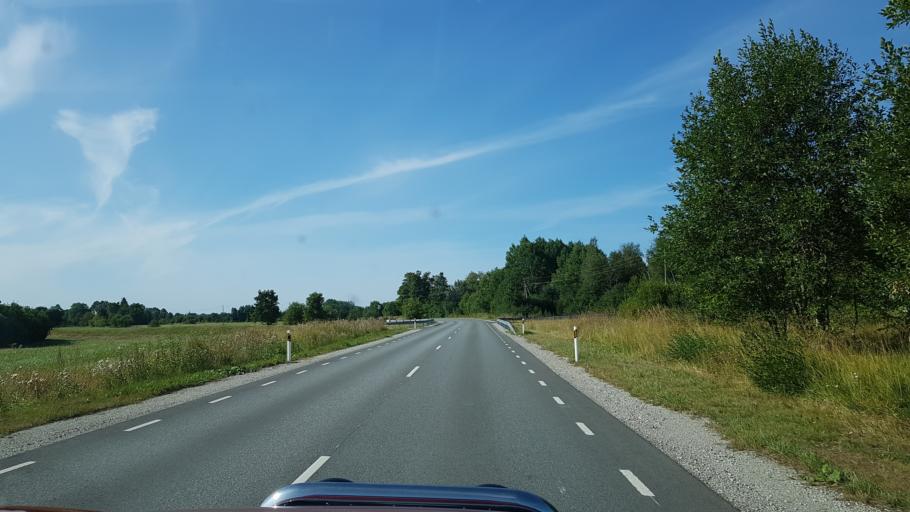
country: EE
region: Harju
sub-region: Rae vald
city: Jueri
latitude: 59.3774
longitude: 24.9276
